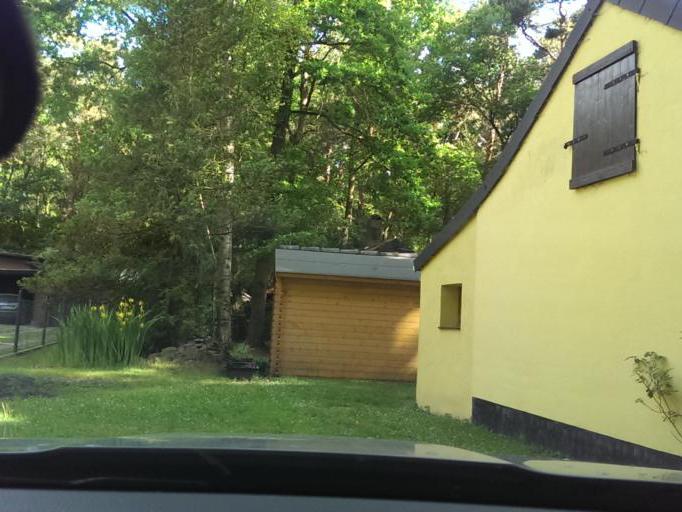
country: DE
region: Lower Saxony
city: Elze
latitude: 52.5663
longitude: 9.7298
